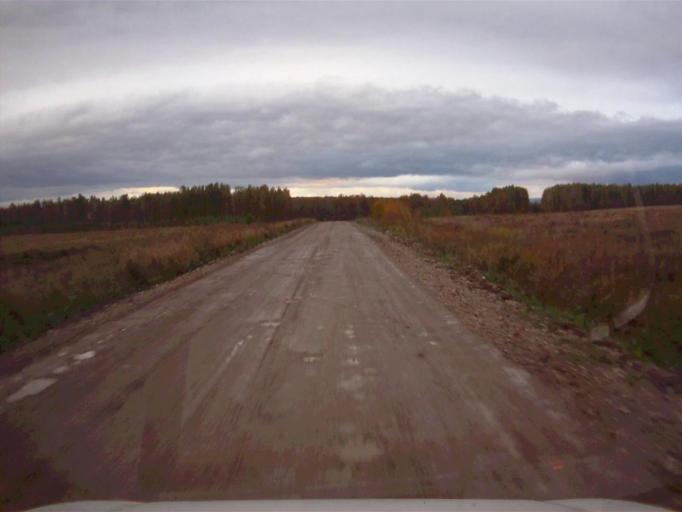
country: RU
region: Sverdlovsk
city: Mikhaylovsk
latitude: 56.1877
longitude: 59.1872
